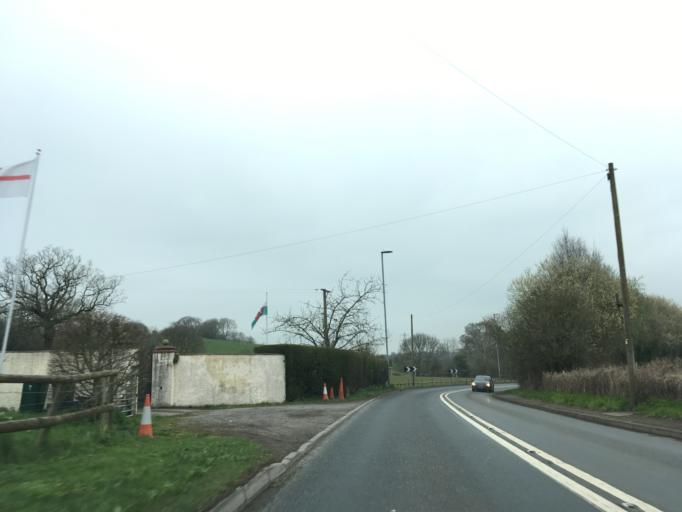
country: GB
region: Wales
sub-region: Newport
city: Caerleon
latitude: 51.6198
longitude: -2.9454
